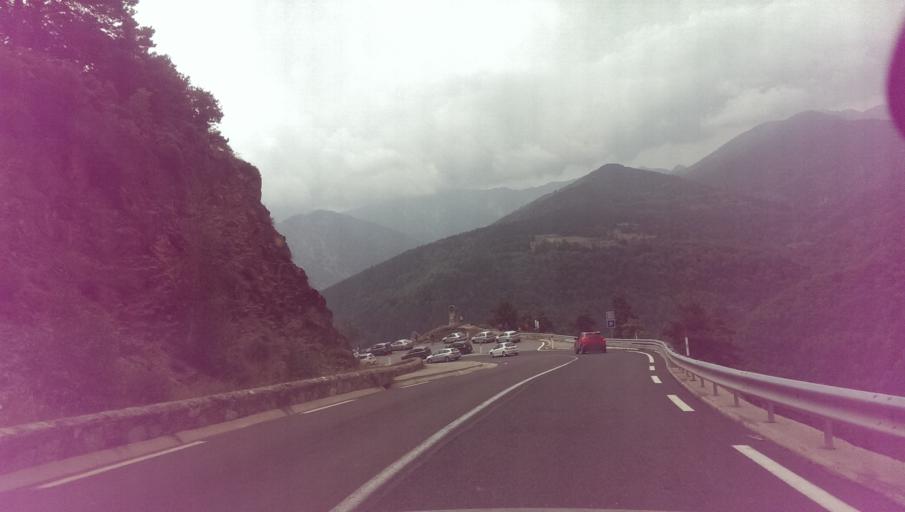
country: ES
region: Catalonia
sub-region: Provincia de Girona
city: Llivia
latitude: 42.5070
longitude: 2.1439
